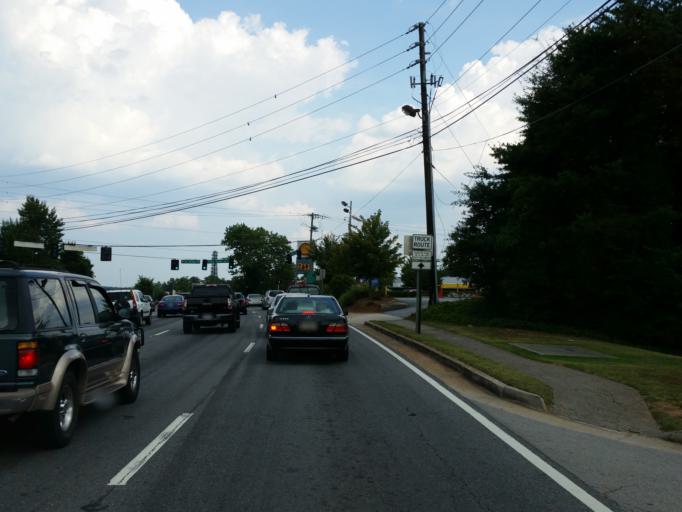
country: US
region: Georgia
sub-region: Fulton County
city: Roswell
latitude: 34.0334
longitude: -84.3417
